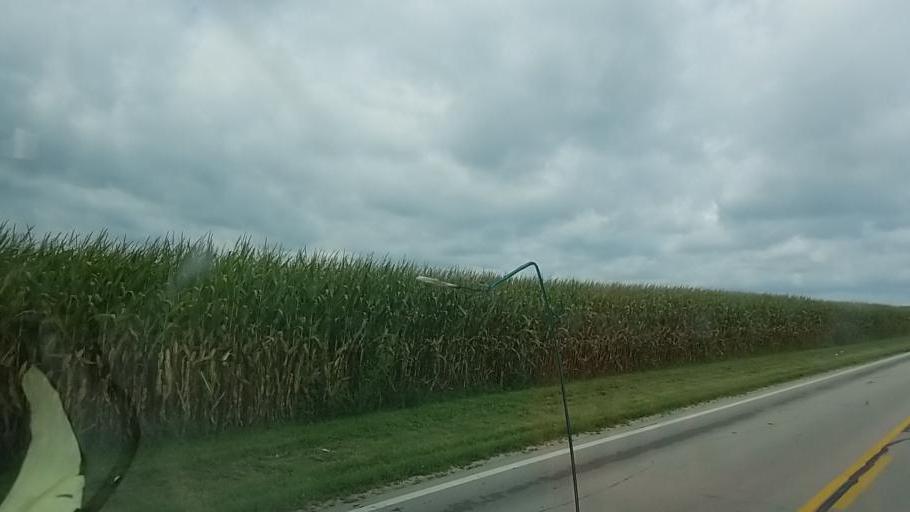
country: US
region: Ohio
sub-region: Madison County
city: Mount Sterling
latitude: 39.7558
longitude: -83.1928
